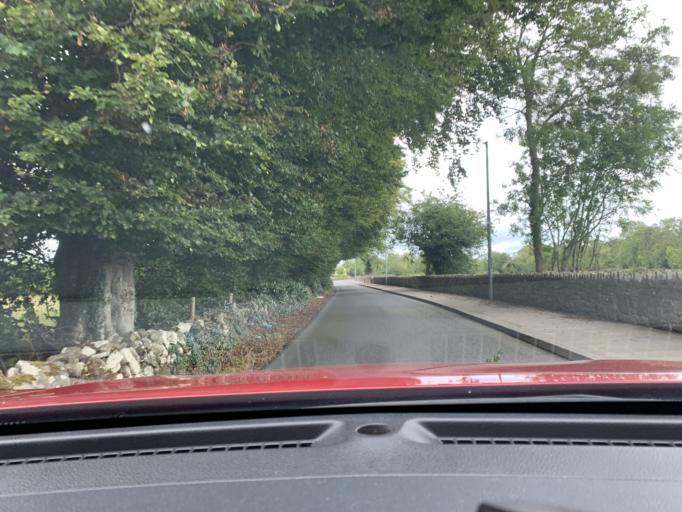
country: IE
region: Connaught
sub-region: Roscommon
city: Boyle
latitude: 53.9817
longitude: -8.2889
